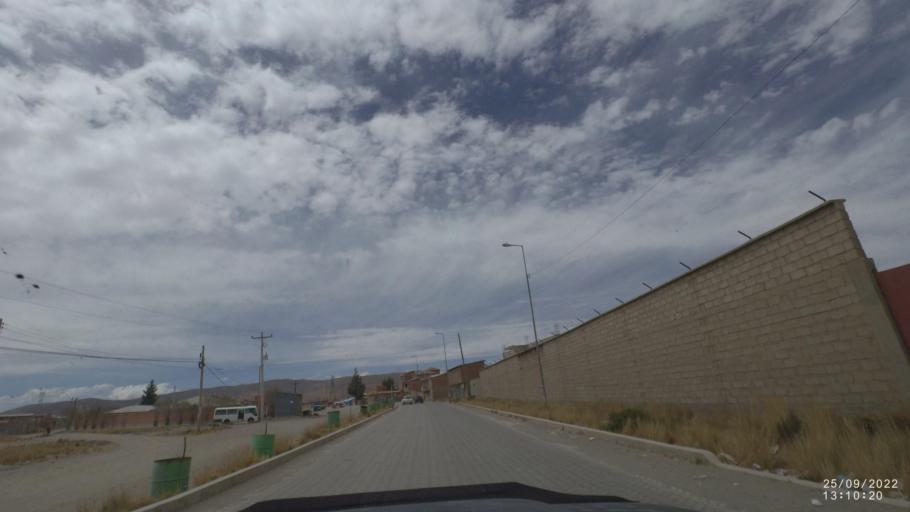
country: BO
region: Oruro
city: Oruro
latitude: -17.9719
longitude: -67.0498
